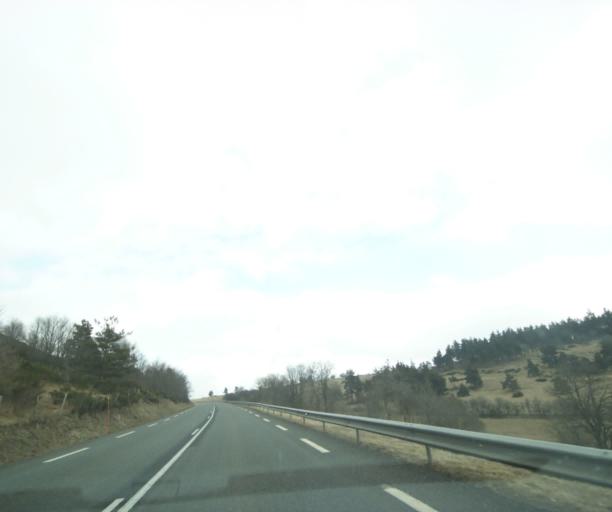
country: FR
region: Languedoc-Roussillon
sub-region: Departement de la Lozere
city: Langogne
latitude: 44.6385
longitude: 3.6957
